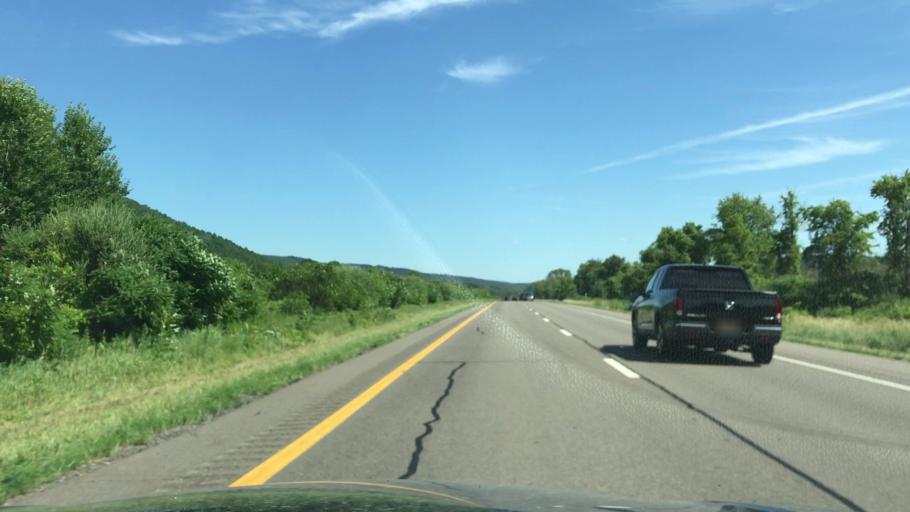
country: US
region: New York
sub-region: Steuben County
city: Bath
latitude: 42.2542
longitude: -77.2080
